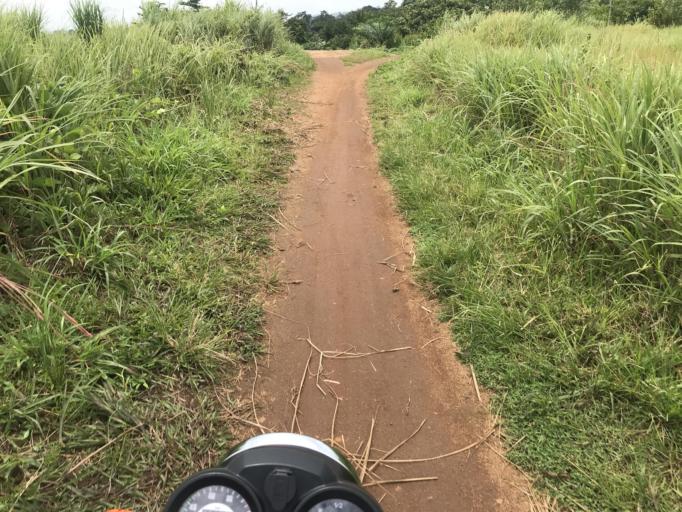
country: GN
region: Nzerekore
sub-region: Prefecture de Guekedou
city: Gueckedou
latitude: 8.4953
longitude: -10.3240
